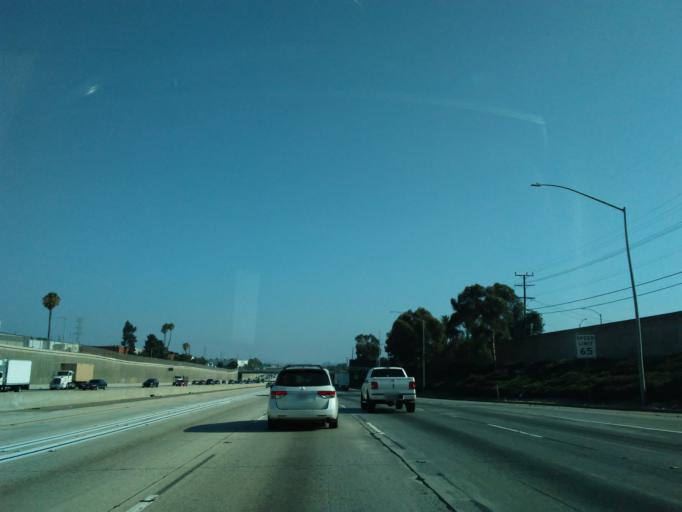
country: US
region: California
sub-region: Los Angeles County
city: West Athens
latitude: 33.9132
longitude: -118.2868
